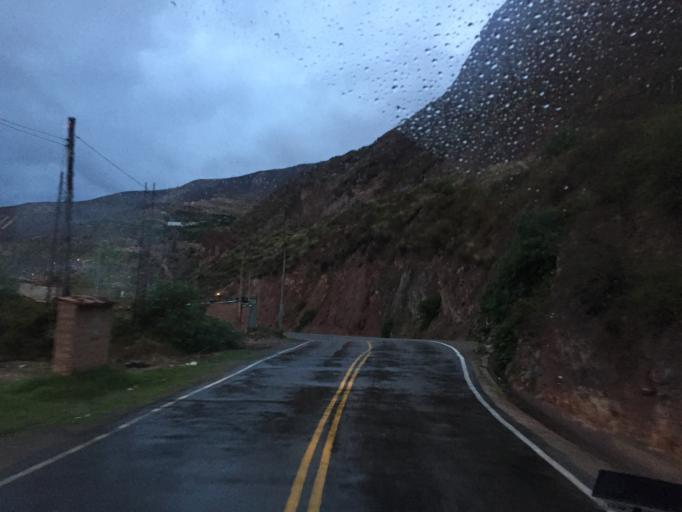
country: PE
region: Cusco
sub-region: Provincia de Urubamba
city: Urubamba
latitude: -13.3114
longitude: -72.1198
